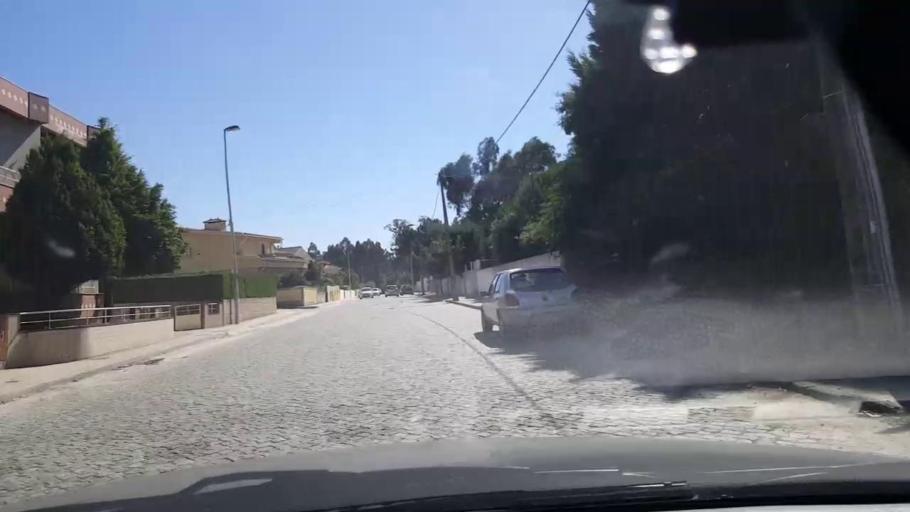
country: PT
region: Porto
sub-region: Vila do Conde
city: Arvore
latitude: 41.3307
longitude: -8.7298
